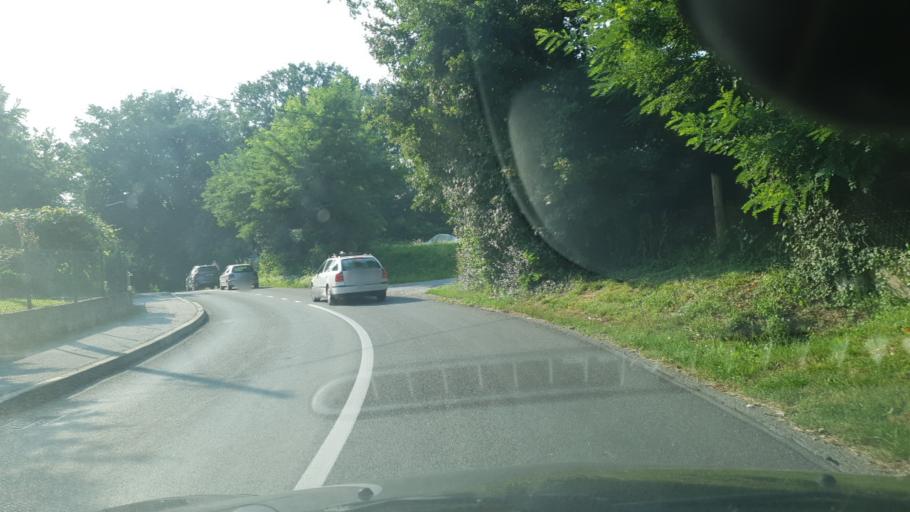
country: HR
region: Krapinsko-Zagorska
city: Oroslavje
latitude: 45.9976
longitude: 15.8944
